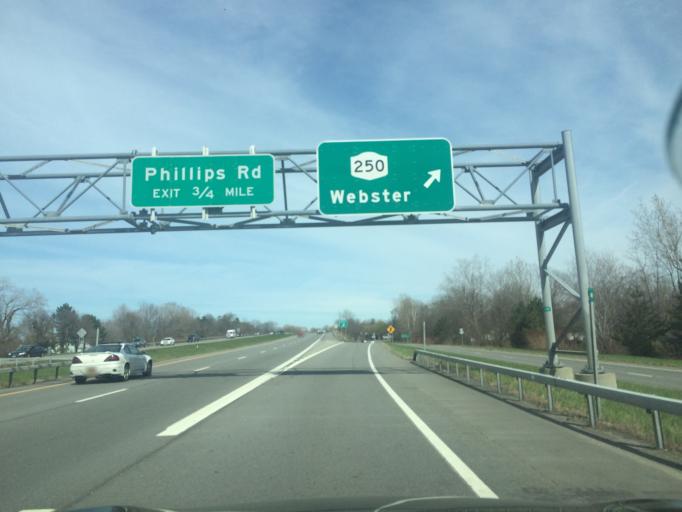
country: US
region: New York
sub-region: Monroe County
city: Webster
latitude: 43.2154
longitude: -77.4352
